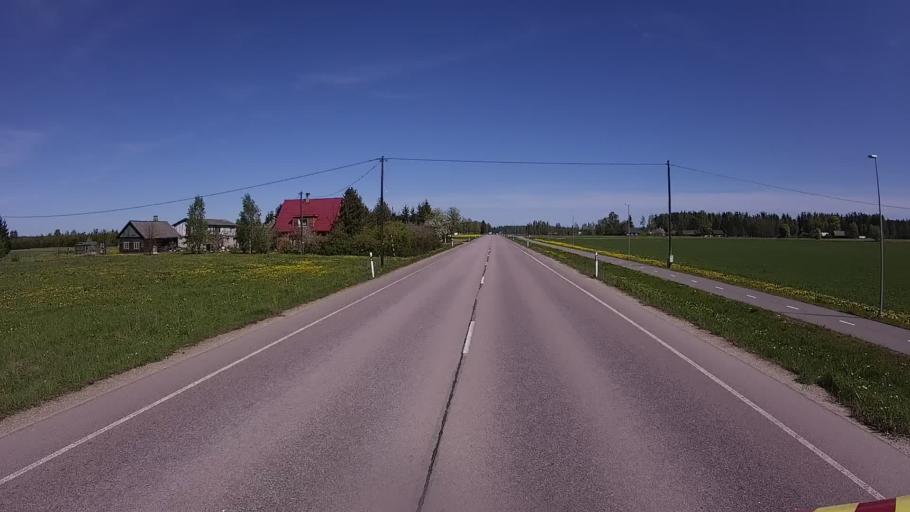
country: EE
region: Polvamaa
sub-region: Polva linn
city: Polva
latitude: 58.0802
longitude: 27.0897
